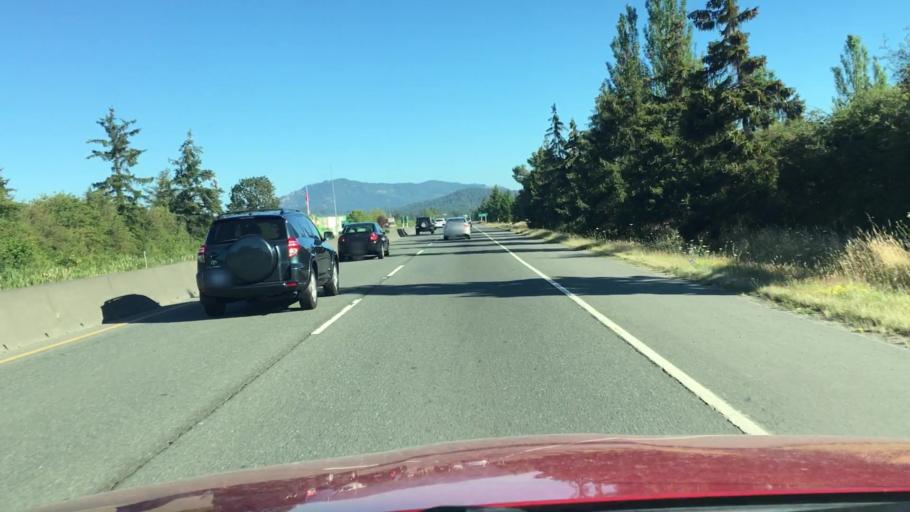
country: CA
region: British Columbia
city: North Saanich
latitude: 48.6522
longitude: -123.4094
